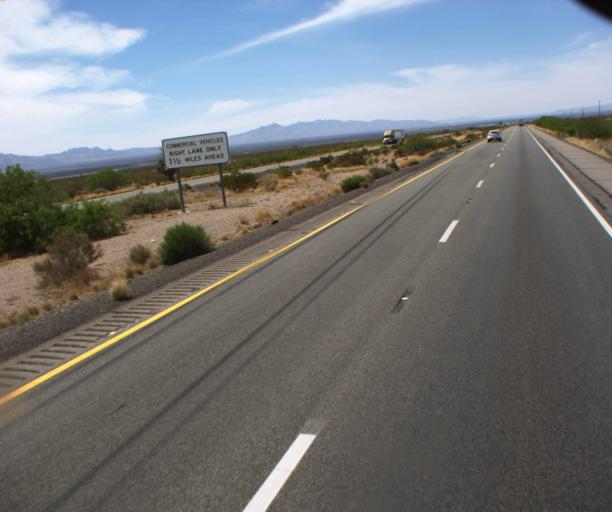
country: US
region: New Mexico
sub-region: Hidalgo County
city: Lordsburg
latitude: 32.2443
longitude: -109.1209
